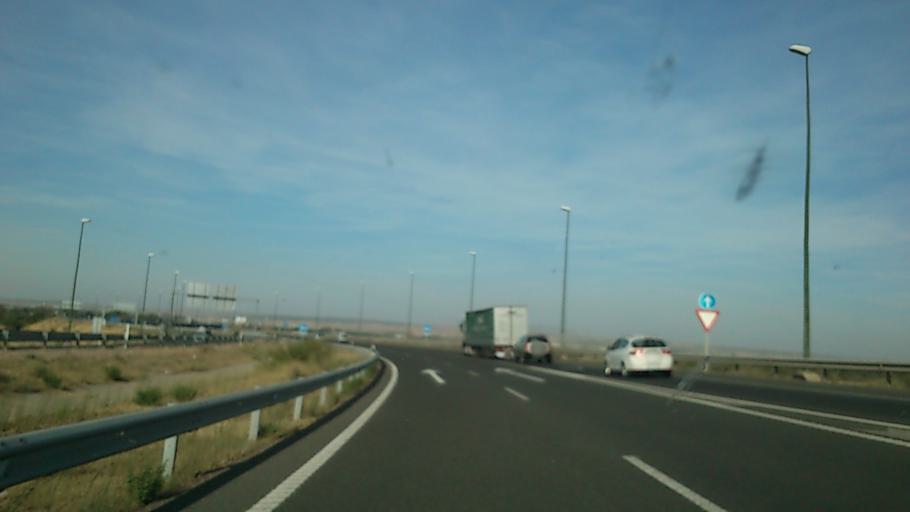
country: ES
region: Aragon
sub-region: Provincia de Zaragoza
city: Zaragoza
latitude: 41.6261
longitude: -0.8458
